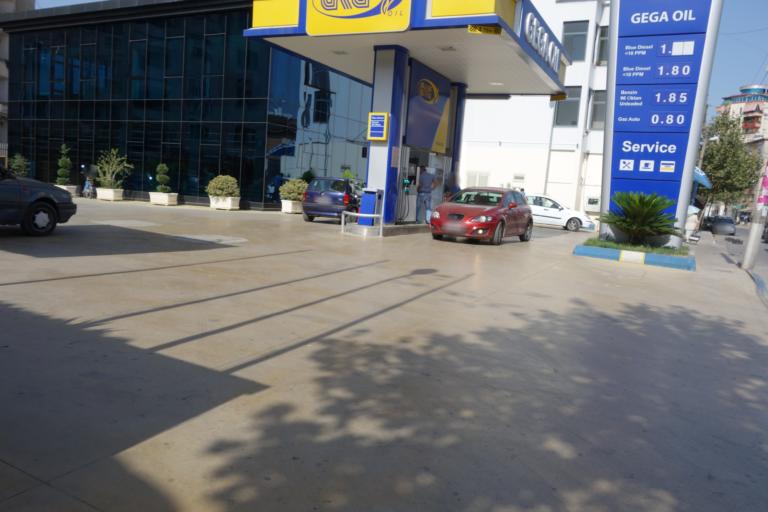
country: AL
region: Tirane
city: Tirana
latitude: 41.3275
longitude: 19.8332
